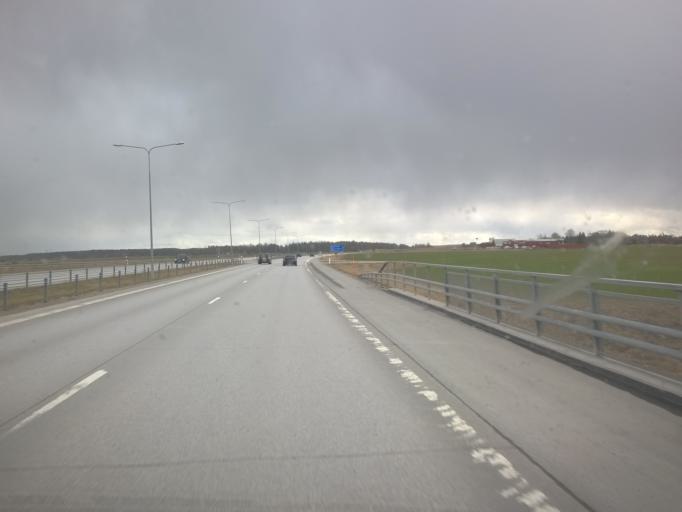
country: SE
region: Uppsala
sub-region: Uppsala Kommun
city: Saevja
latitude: 59.8535
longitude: 17.7325
